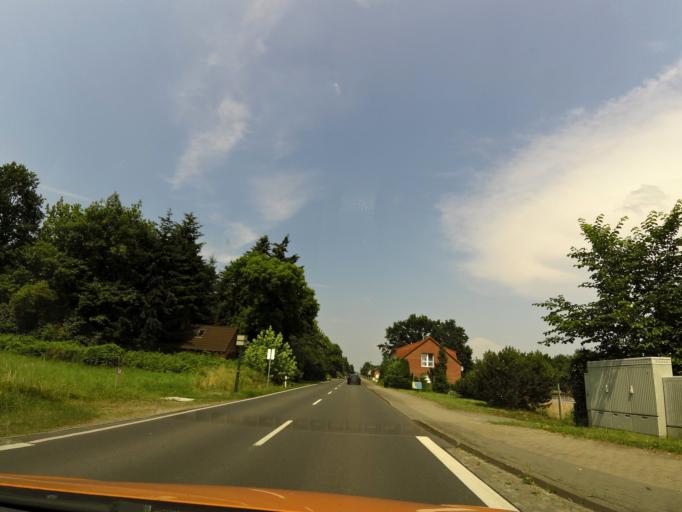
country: DE
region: Brandenburg
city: Pritzwalk
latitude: 53.1926
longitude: 12.1976
